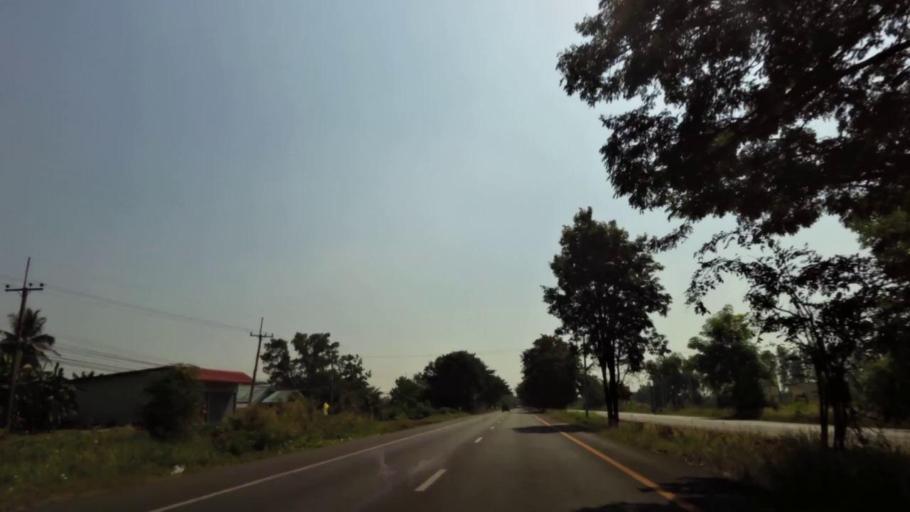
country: TH
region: Nakhon Sawan
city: Kao Liao
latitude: 15.9730
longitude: 100.1192
